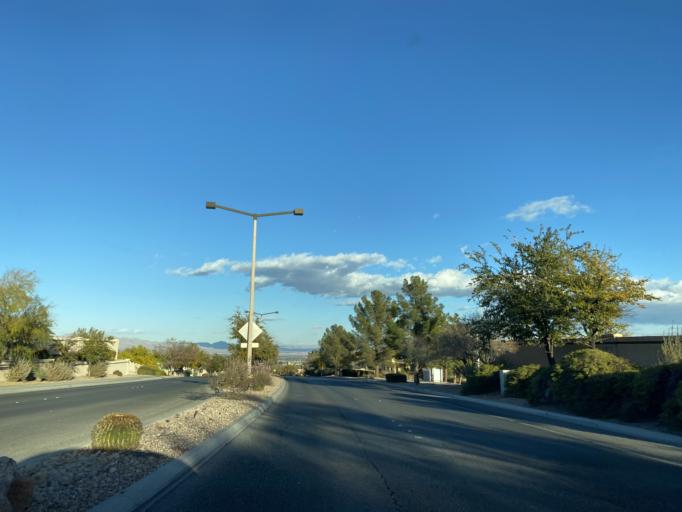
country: US
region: Nevada
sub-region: Clark County
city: Summerlin South
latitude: 36.2040
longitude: -115.3281
